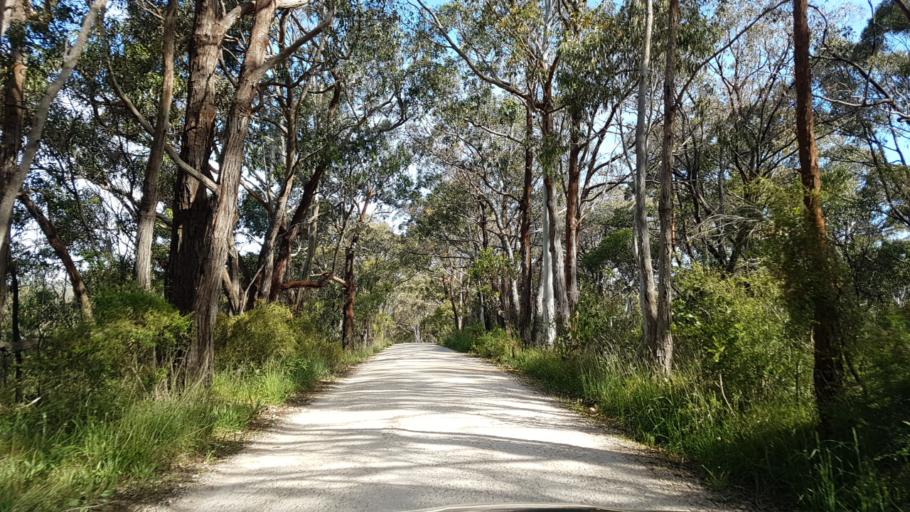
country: AU
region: South Australia
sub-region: Adelaide Hills
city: Adelaide Hills
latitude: -34.9076
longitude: 138.7483
